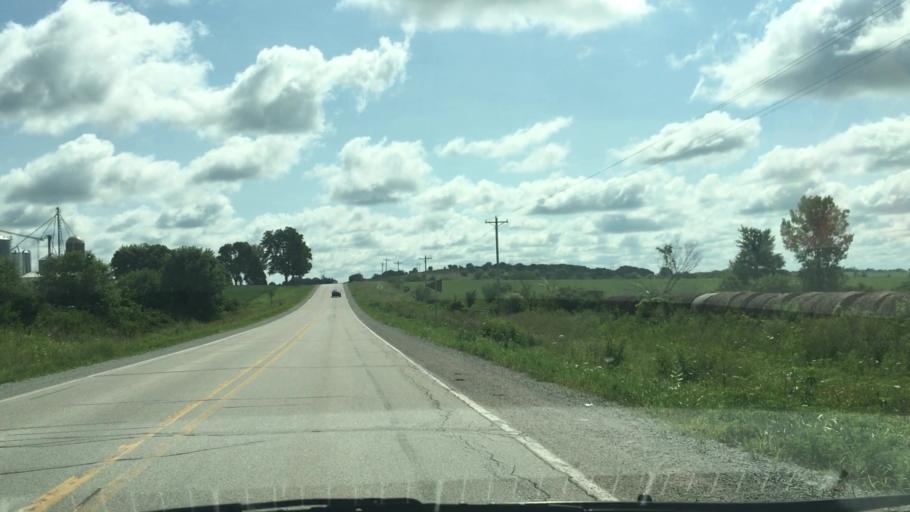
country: US
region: Iowa
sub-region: Johnson County
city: Solon
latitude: 41.8313
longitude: -91.4970
